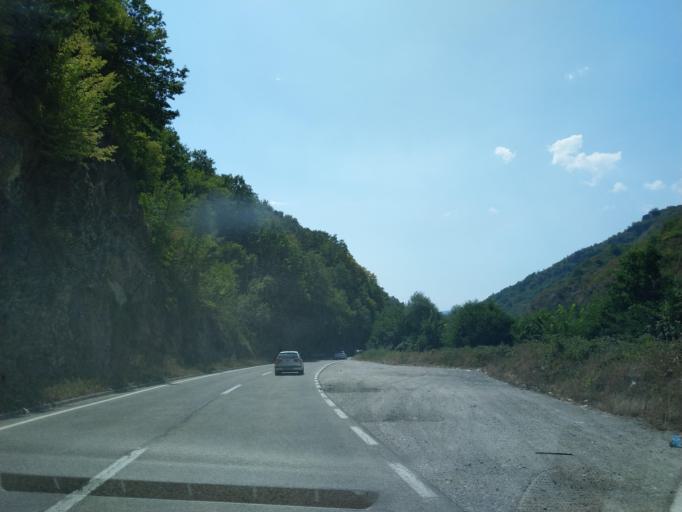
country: RS
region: Central Serbia
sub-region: Zlatiborski Okrug
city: Prijepolje
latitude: 43.4608
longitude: 19.6468
